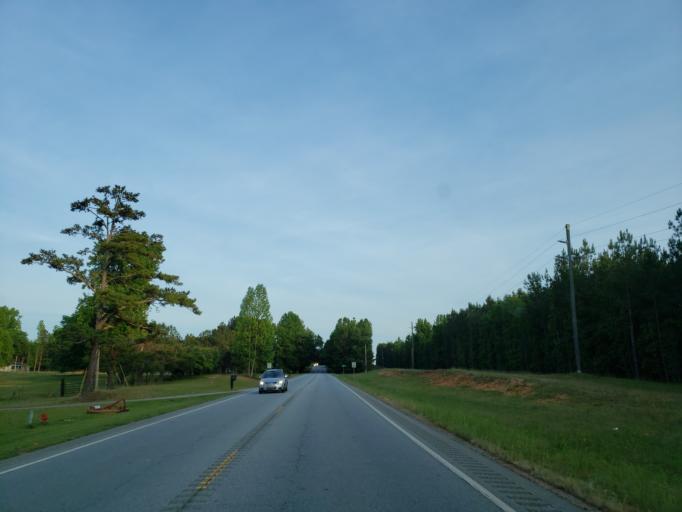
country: US
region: Georgia
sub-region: Coweta County
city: Newnan
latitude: 33.4424
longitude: -84.8776
